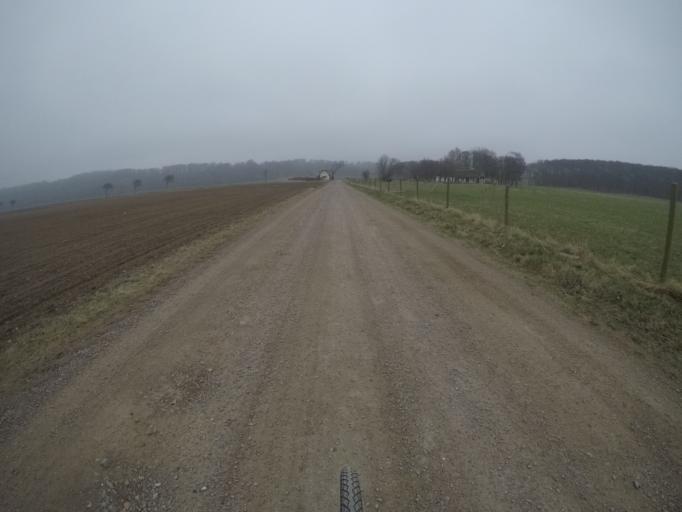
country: SE
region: Skane
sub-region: Hoganas Kommun
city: Hoganas
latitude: 56.2709
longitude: 12.5194
